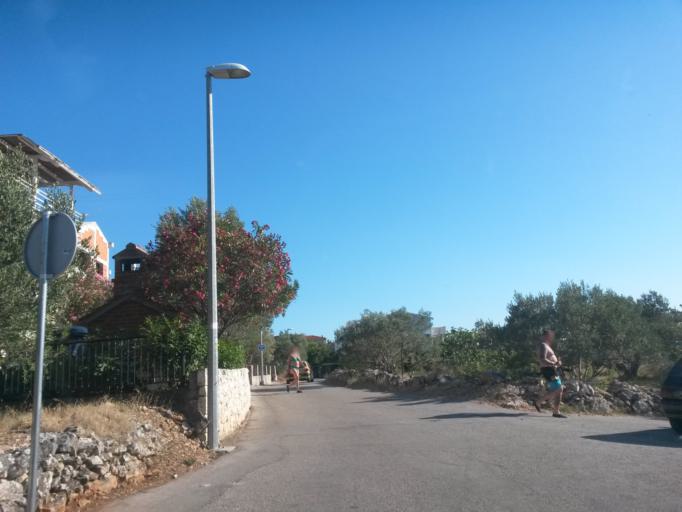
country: HR
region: Sibensko-Kniniska
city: Rogoznica
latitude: 43.5402
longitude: 15.9609
